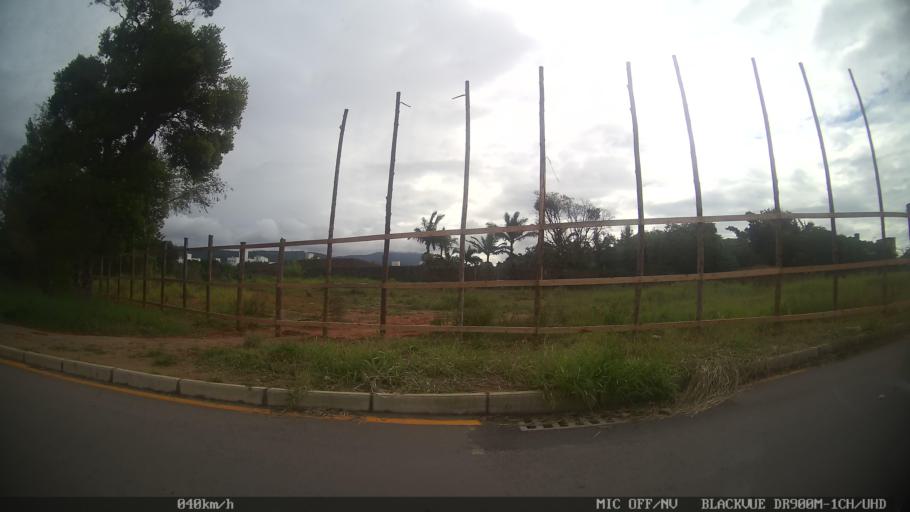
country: BR
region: Santa Catarina
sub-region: Sao Jose
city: Campinas
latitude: -27.5466
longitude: -48.6303
